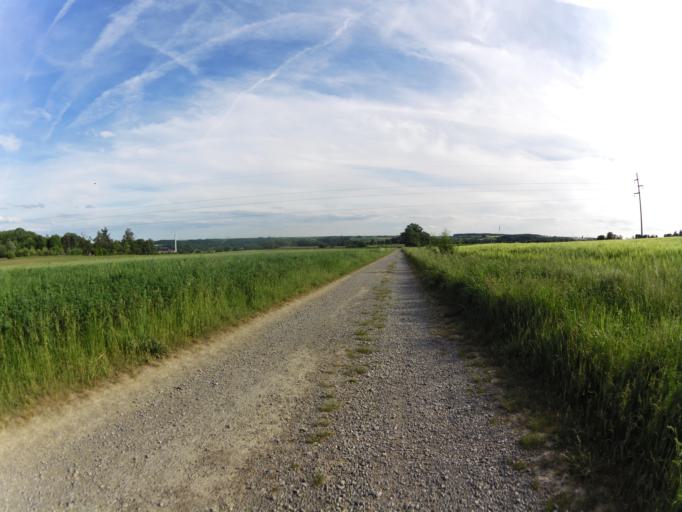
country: DE
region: Bavaria
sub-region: Regierungsbezirk Unterfranken
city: Ochsenfurt
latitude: 49.6778
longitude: 10.0716
